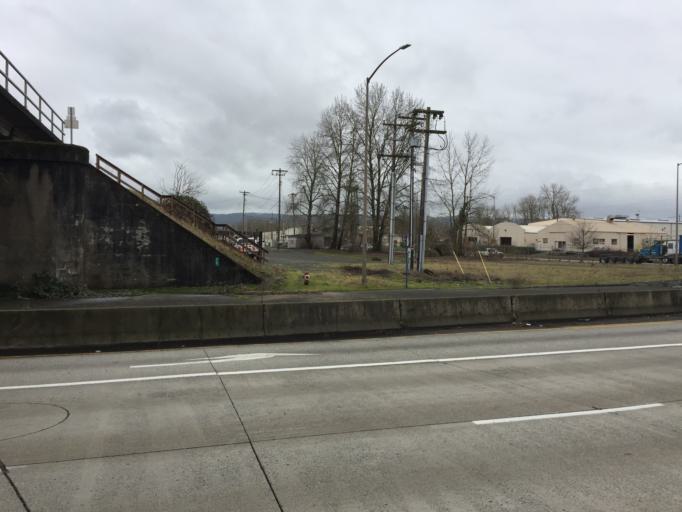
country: US
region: Washington
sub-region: Clark County
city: Vancouver
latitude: 45.6135
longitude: -122.7033
